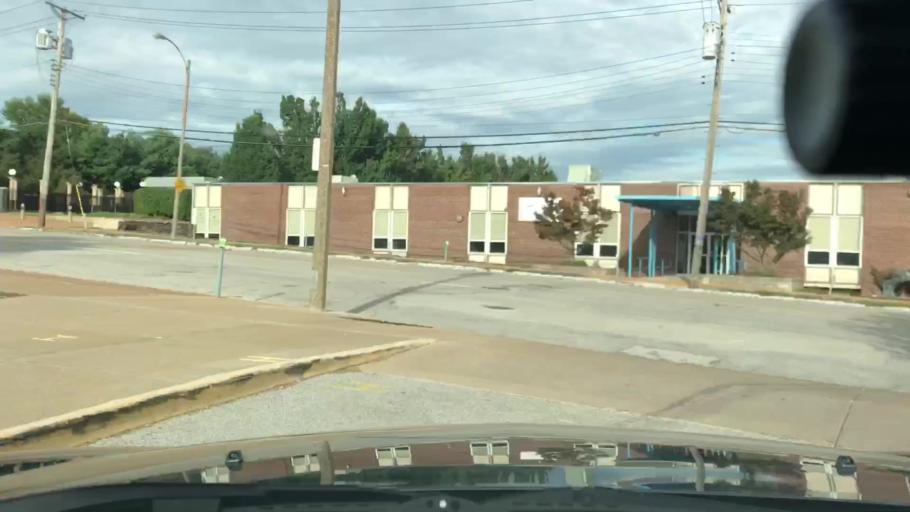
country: US
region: Missouri
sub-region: Saint Louis County
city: Richmond Heights
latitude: 38.6260
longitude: -90.2755
